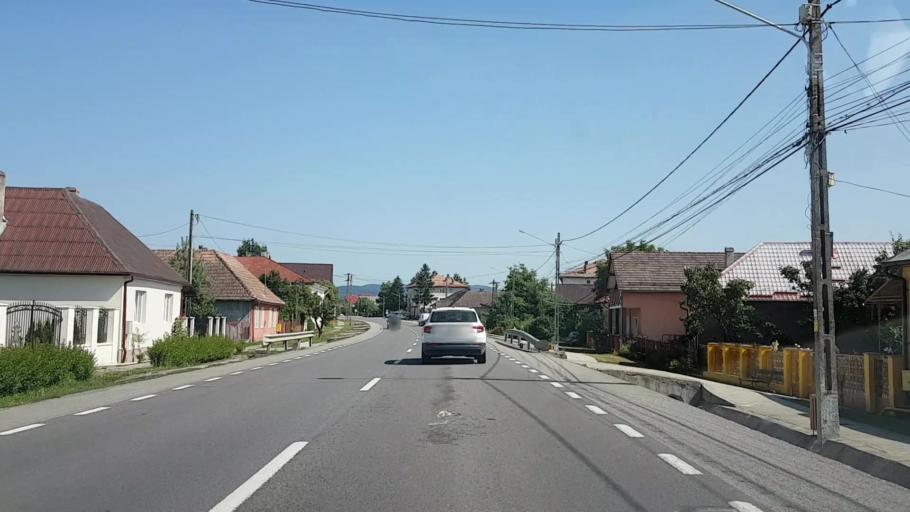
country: RO
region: Bistrita-Nasaud
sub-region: Comuna Sieu-Magherus
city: Sieu-Magherus
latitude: 47.0925
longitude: 24.3712
